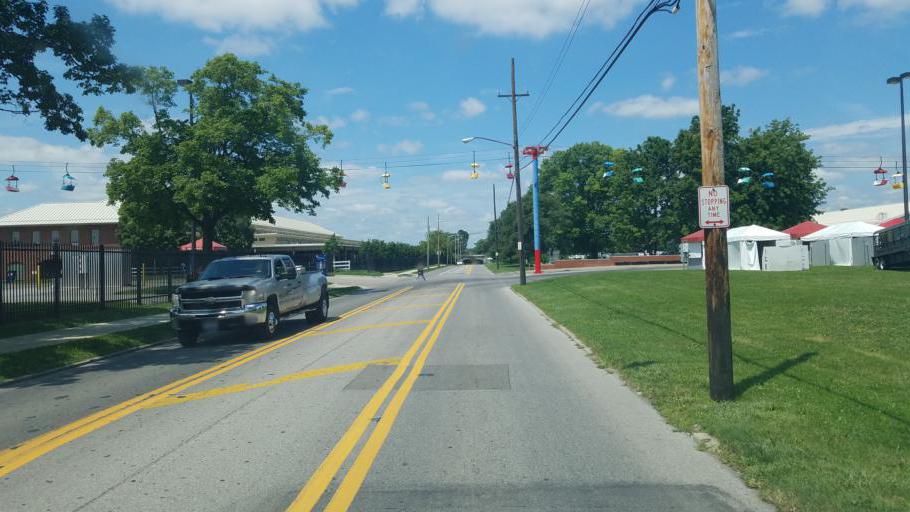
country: US
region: Ohio
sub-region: Franklin County
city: Columbus
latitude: 40.0010
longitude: -82.9903
